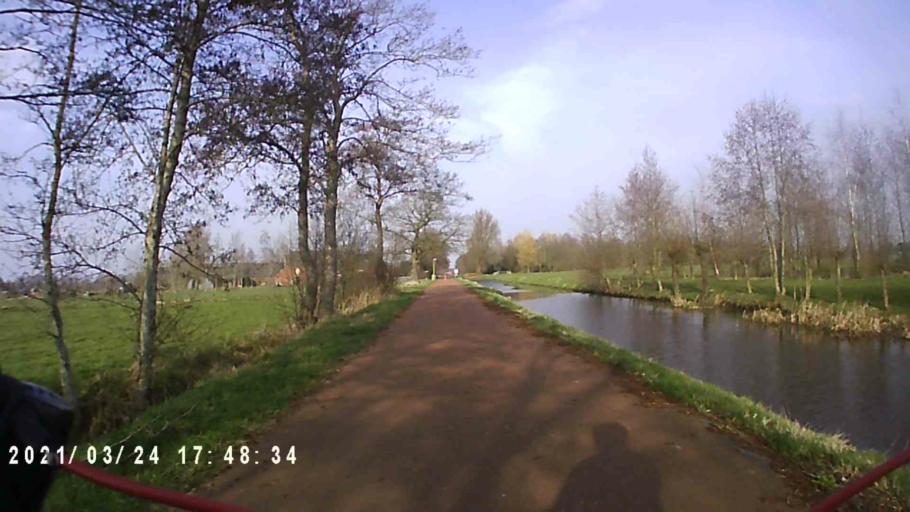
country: NL
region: Groningen
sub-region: Gemeente Leek
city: Leek
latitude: 53.1185
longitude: 6.3370
